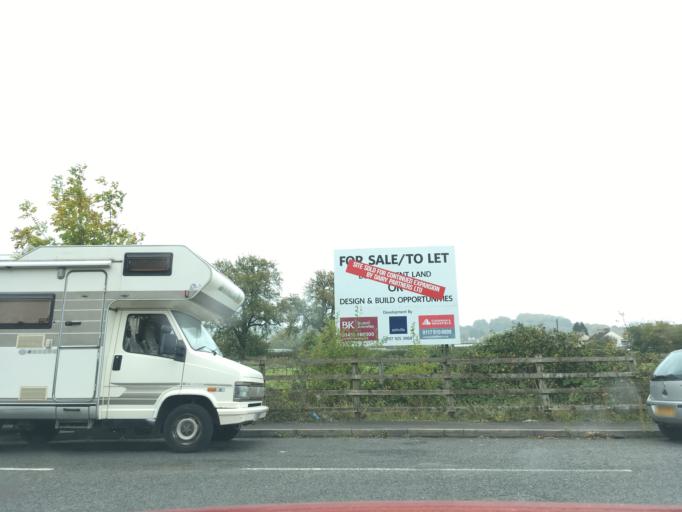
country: GB
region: England
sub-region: Gloucestershire
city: Stonehouse
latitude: 51.7528
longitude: -2.2917
